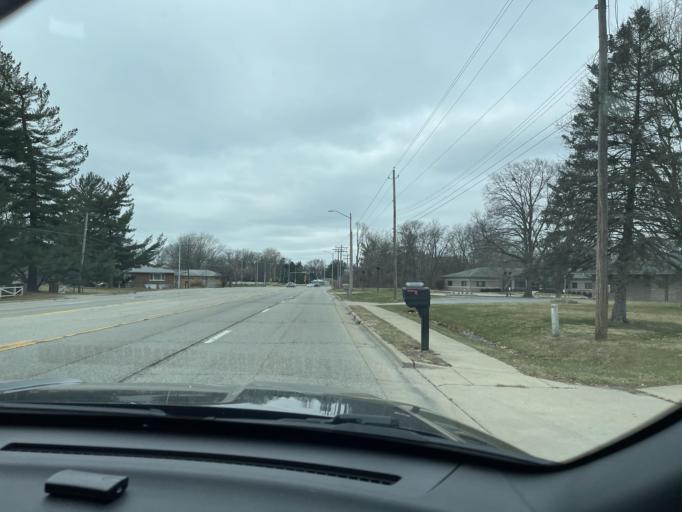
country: US
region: Illinois
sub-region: Sangamon County
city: Leland Grove
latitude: 39.8111
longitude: -89.6919
